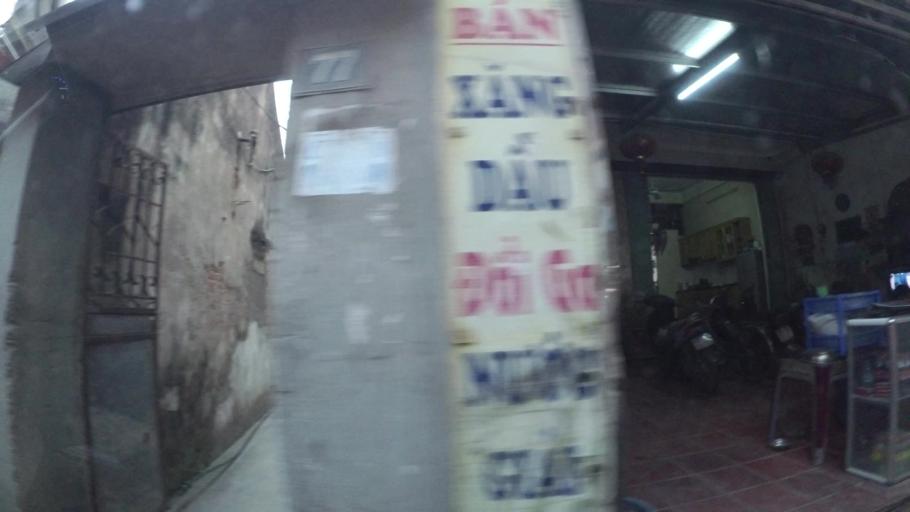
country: VN
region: Ha Noi
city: Thanh Xuan
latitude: 20.9802
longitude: 105.8034
